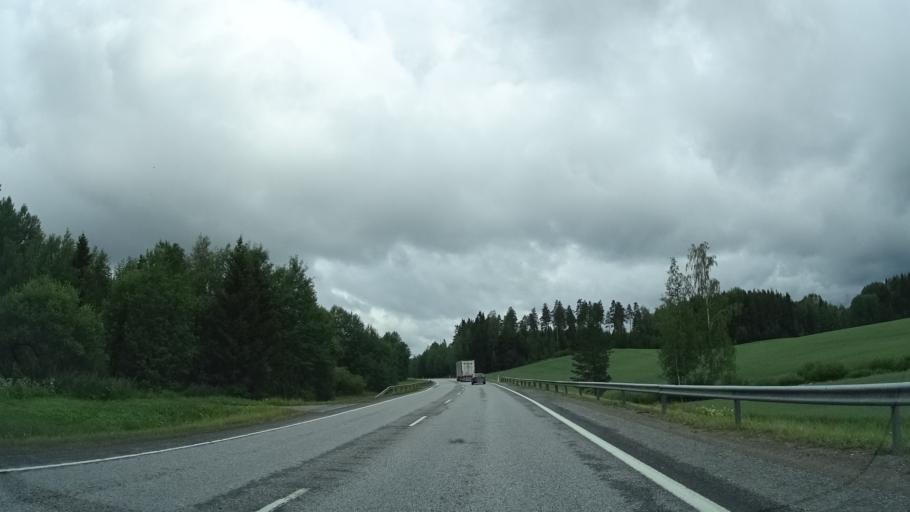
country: FI
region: Uusimaa
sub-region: Helsinki
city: Vihti
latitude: 60.4502
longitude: 24.3236
